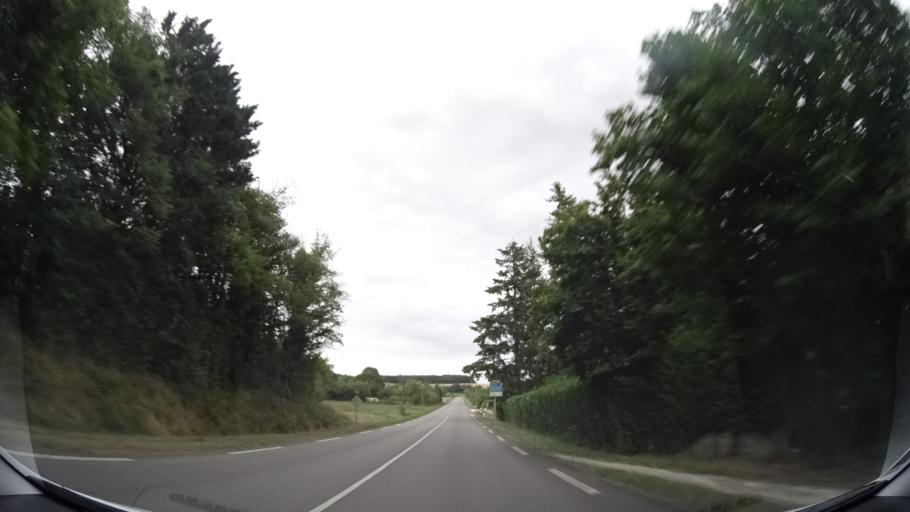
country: FR
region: Centre
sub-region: Departement du Loiret
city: Douchy
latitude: 47.9354
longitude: 3.0839
